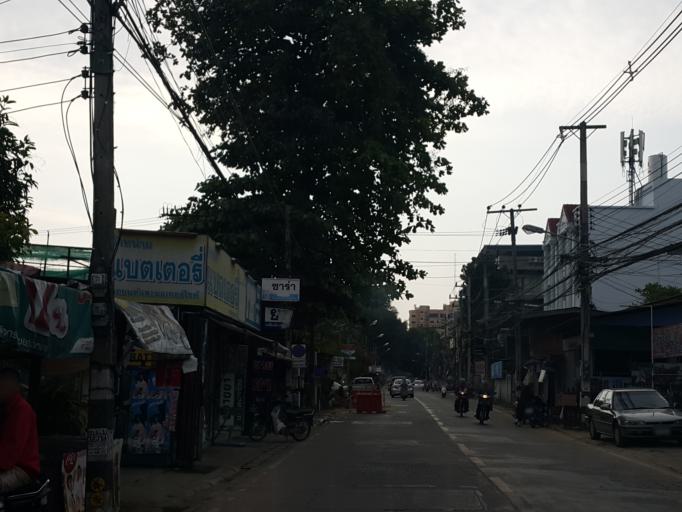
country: TH
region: Chiang Mai
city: Chiang Mai
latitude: 18.7973
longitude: 99.0159
